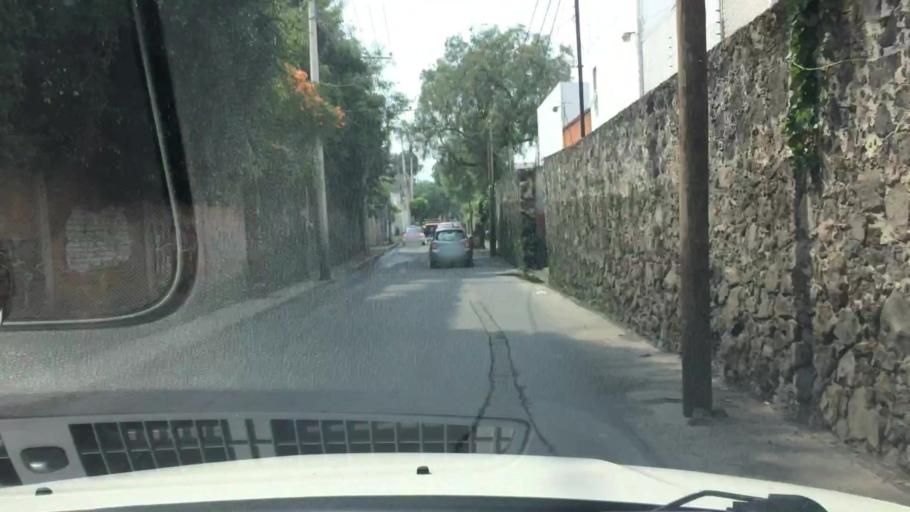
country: MX
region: Mexico City
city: Tlalpan
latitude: 19.2708
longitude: -99.1477
